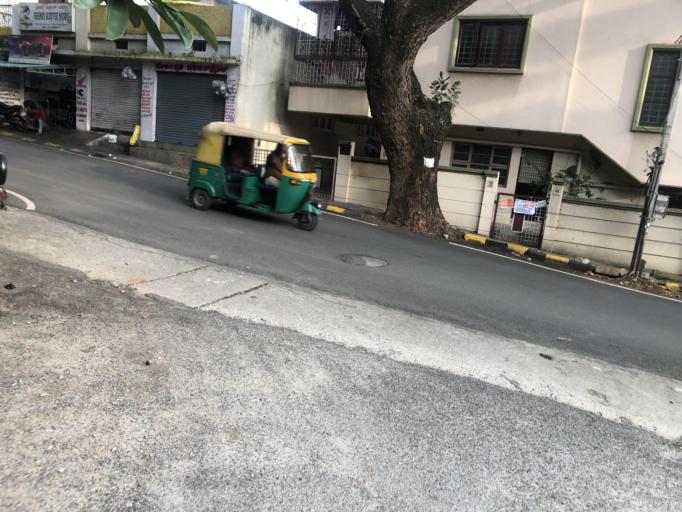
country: IN
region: Karnataka
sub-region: Bangalore Urban
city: Bangalore
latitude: 12.9389
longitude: 77.5468
